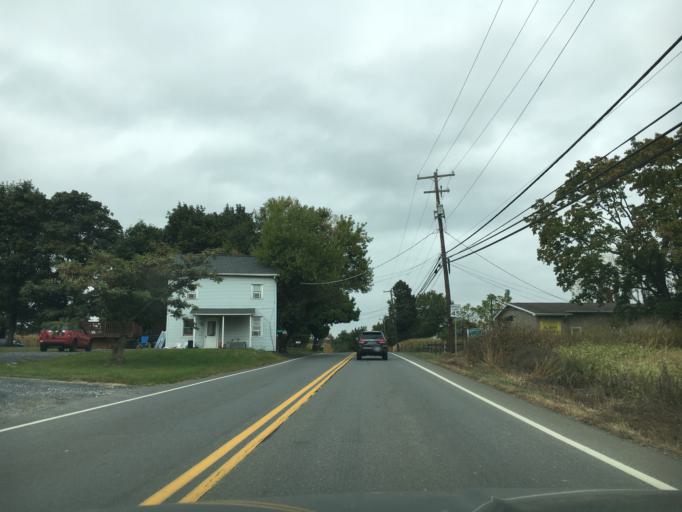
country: US
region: Pennsylvania
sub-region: Northampton County
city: Bath
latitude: 40.6946
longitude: -75.3921
